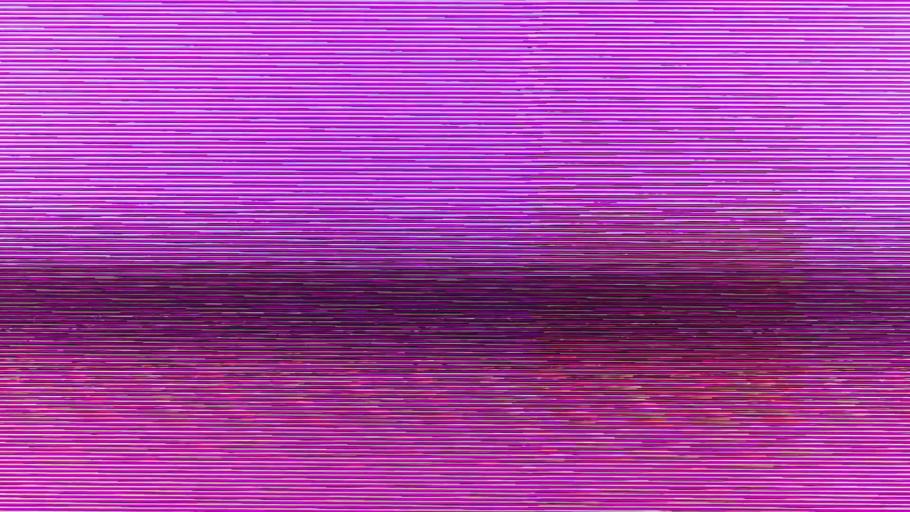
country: US
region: Michigan
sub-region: Wayne County
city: Belleville
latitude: 42.2184
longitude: -83.4848
